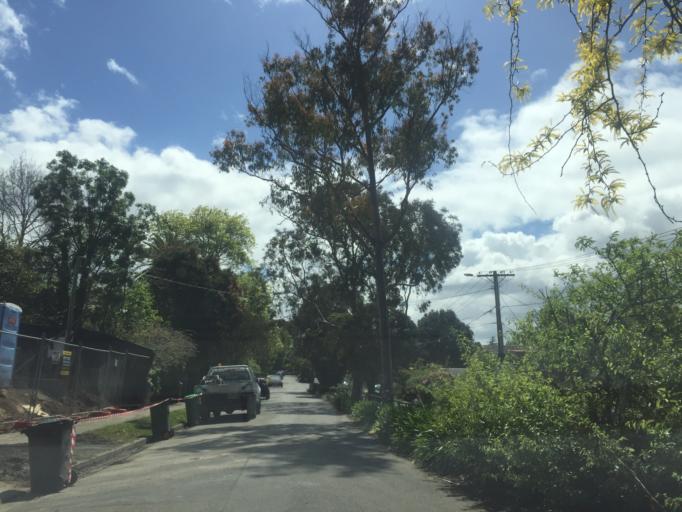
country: AU
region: Victoria
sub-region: Banyule
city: Bellfield
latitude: -37.7663
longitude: 145.0491
